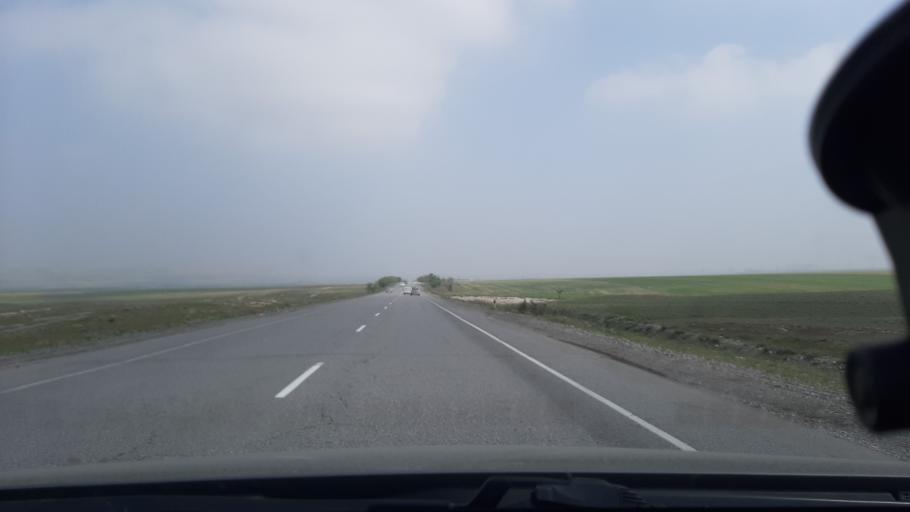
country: UZ
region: Toshkent
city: Bekobod
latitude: 40.1079
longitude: 69.1868
